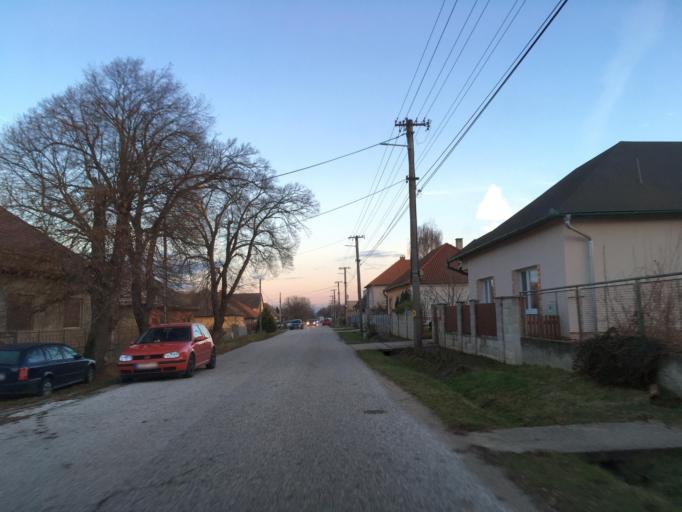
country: SK
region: Nitriansky
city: Svodin
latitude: 47.8675
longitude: 18.4678
